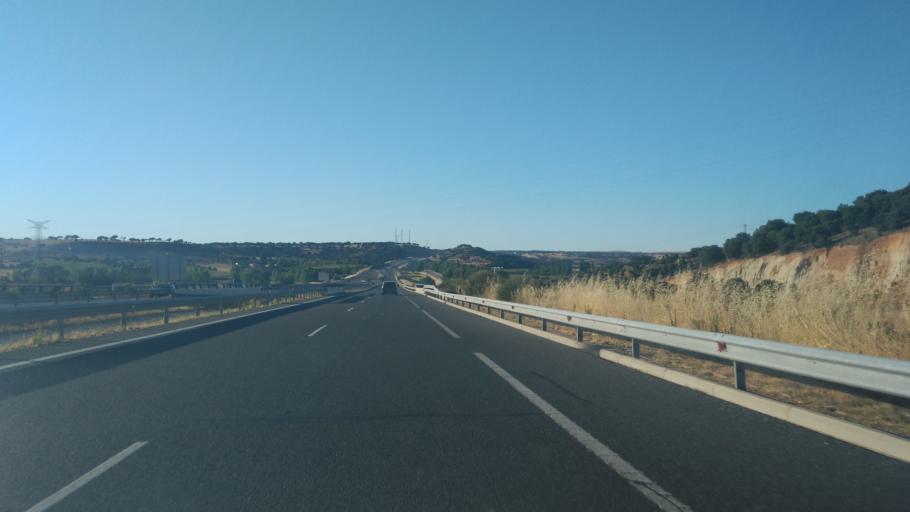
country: ES
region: Castille and Leon
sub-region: Provincia de Salamanca
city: Montejo
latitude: 40.6782
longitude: -5.6198
